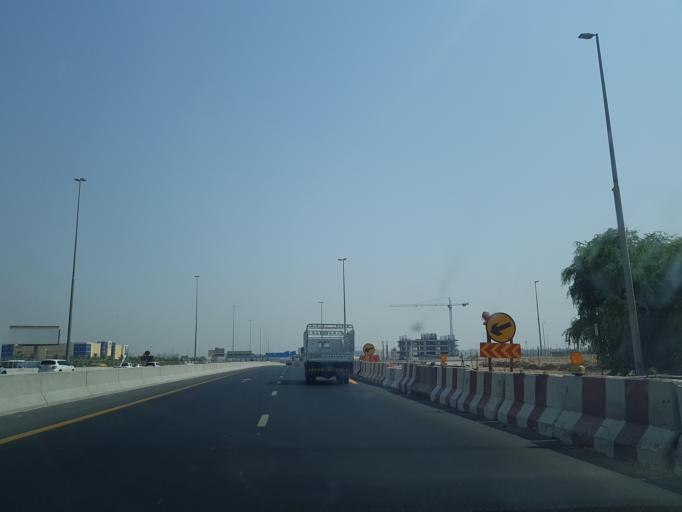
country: AE
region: Ash Shariqah
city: Sharjah
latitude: 25.1659
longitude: 55.3935
